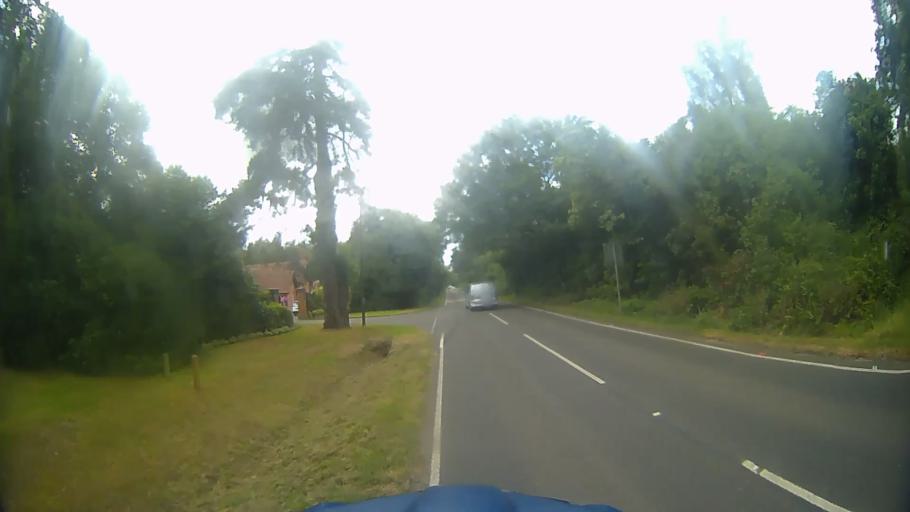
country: GB
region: England
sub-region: Wokingham
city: Winnersh
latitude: 51.4131
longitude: -0.8767
